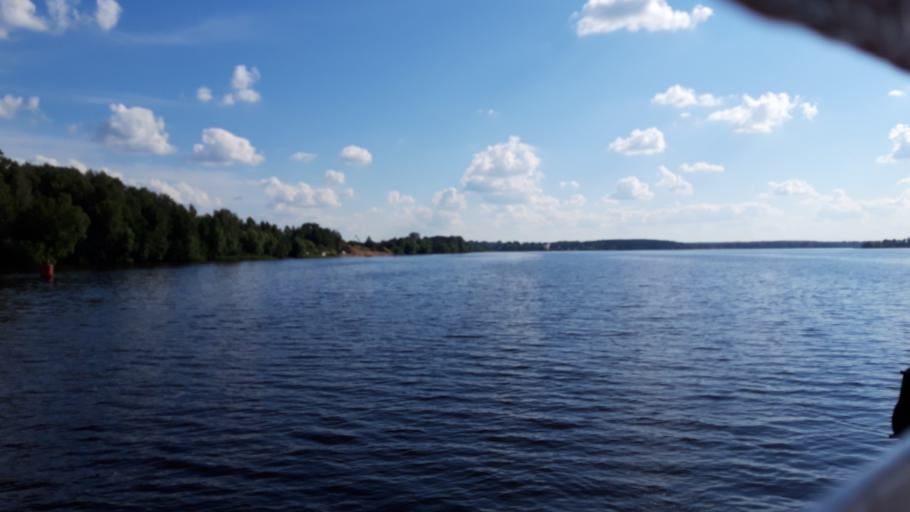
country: RU
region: Tverskaya
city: Zavidovo
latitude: 56.6296
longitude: 36.6036
